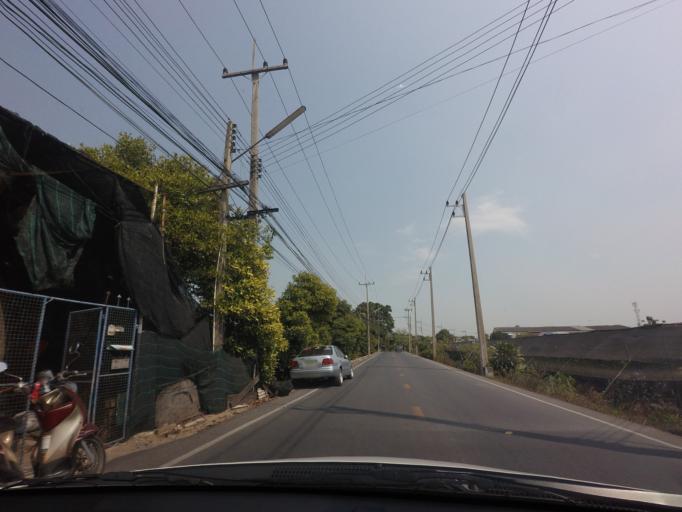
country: TH
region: Samut Sakhon
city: Krathum Baen
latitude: 13.6944
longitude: 100.2497
